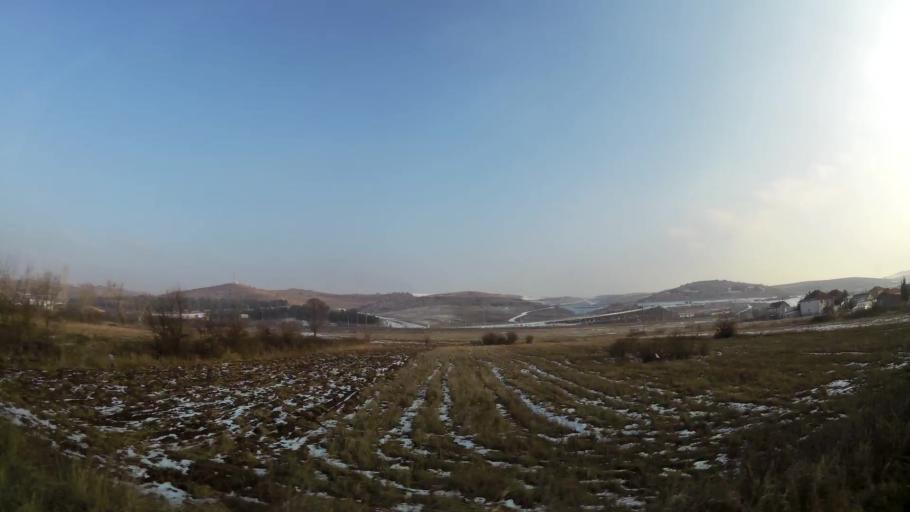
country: MK
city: Miladinovci
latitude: 41.9924
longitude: 21.6548
